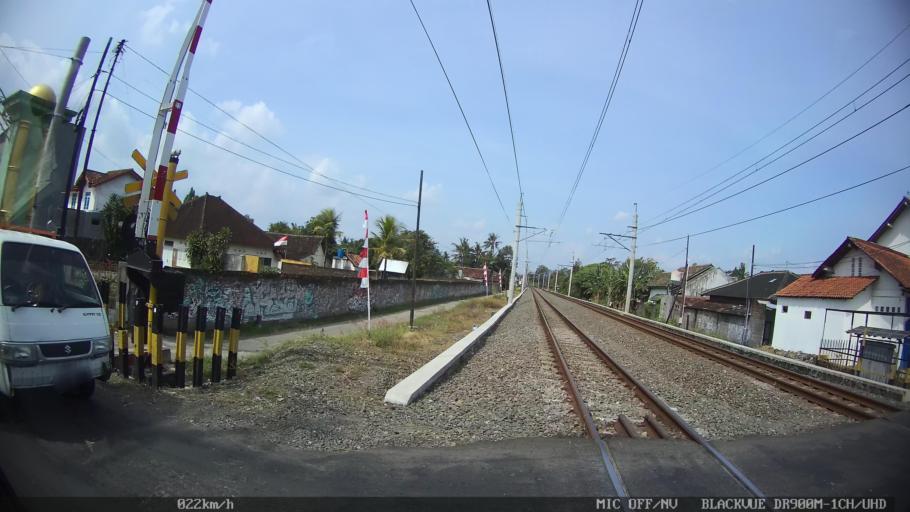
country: ID
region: Daerah Istimewa Yogyakarta
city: Depok
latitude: -7.7844
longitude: 110.4472
